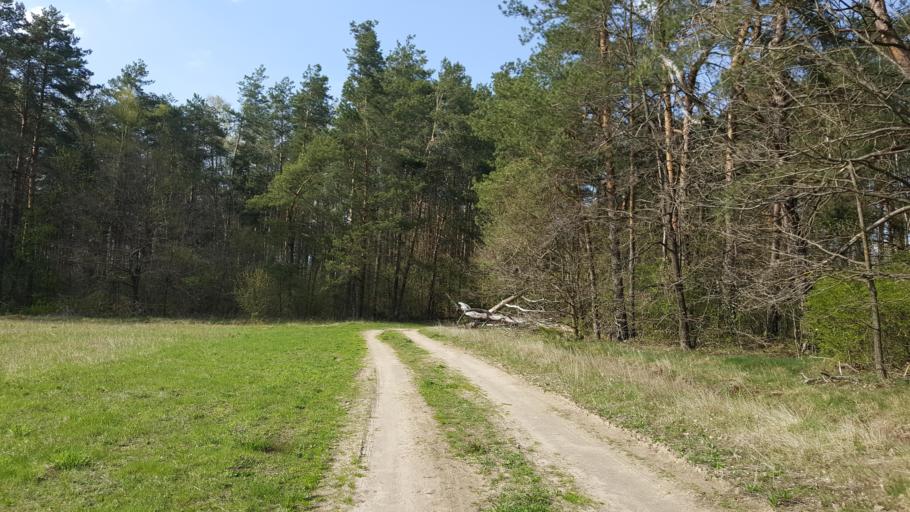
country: BY
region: Brest
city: Kamyanyets
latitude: 52.3285
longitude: 23.8536
